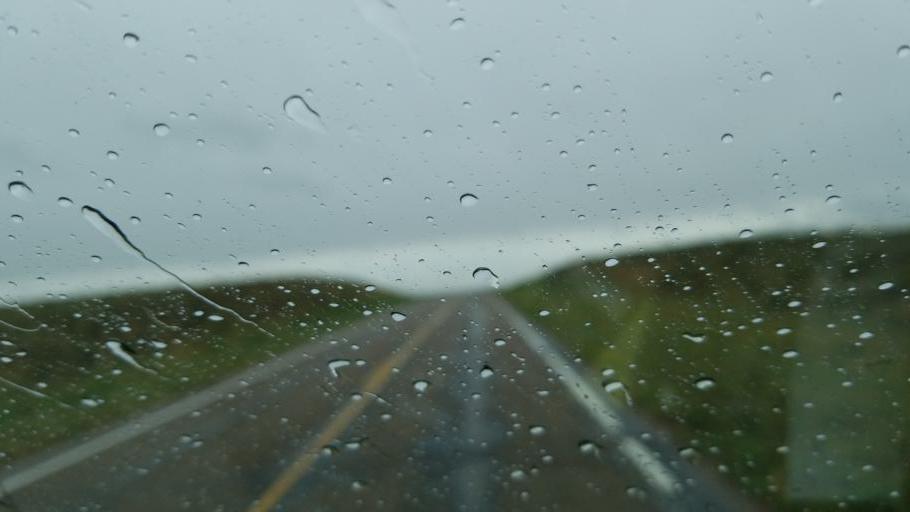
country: US
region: Colorado
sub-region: Lincoln County
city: Hugo
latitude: 38.8498
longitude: -103.2015
